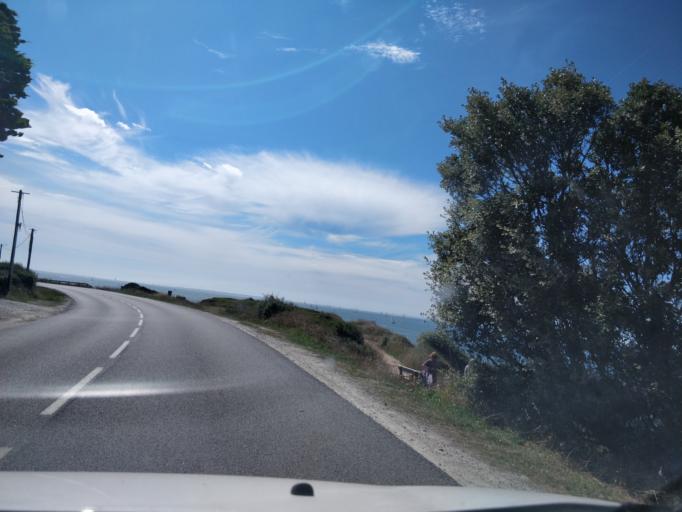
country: FR
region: Brittany
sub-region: Departement du Morbihan
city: Saint-Philibert
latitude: 47.5692
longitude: -3.0071
